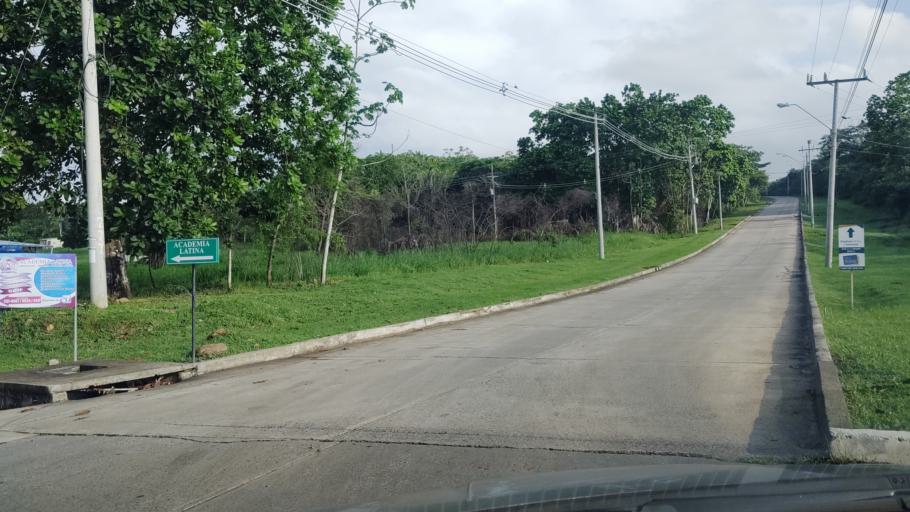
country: PA
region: Panama
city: Nuevo Arraijan
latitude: 8.9206
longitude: -79.7499
